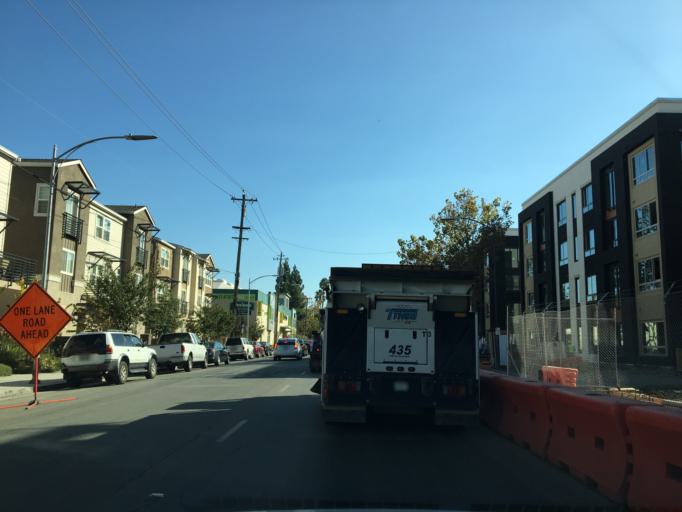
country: US
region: California
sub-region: Santa Clara County
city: San Jose
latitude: 37.3552
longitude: -121.8919
